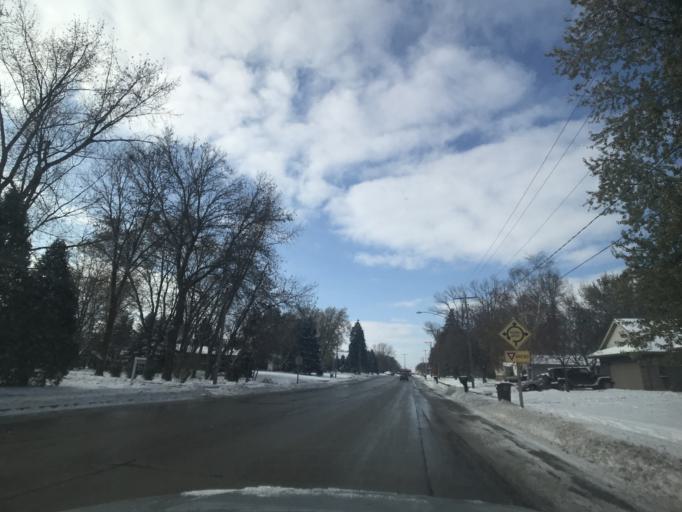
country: US
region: Wisconsin
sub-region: Brown County
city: De Pere
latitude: 44.4451
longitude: -88.0875
